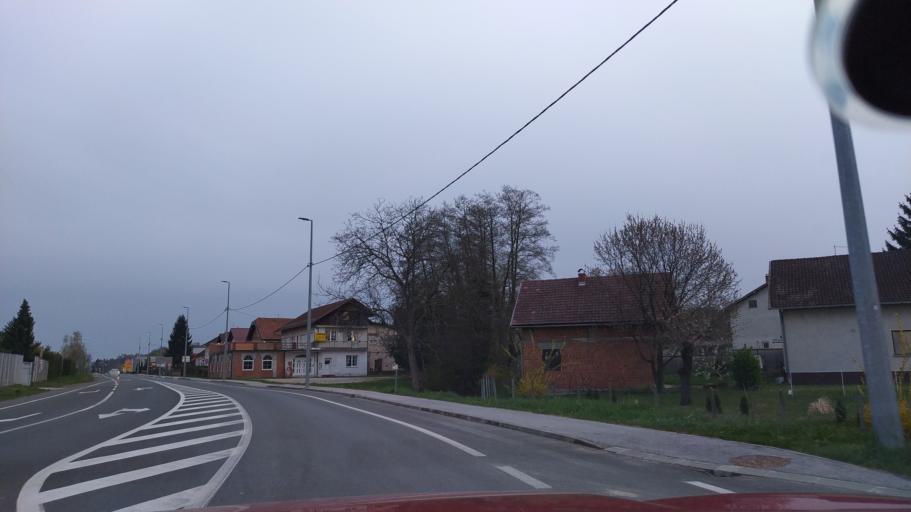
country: HR
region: Varazdinska
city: Ludbreg
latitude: 46.2443
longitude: 16.6238
